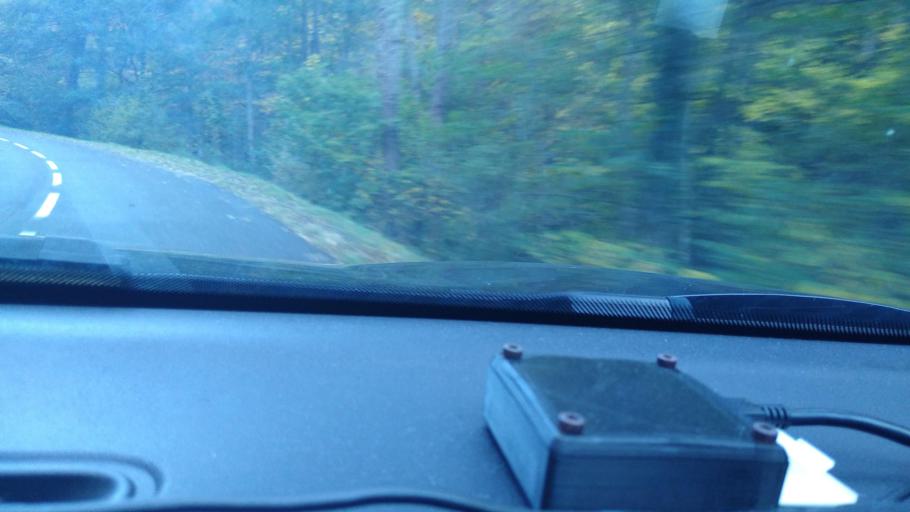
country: FR
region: Languedoc-Roussillon
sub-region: Departement de l'Aude
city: Quillan
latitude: 42.7333
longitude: 2.0970
